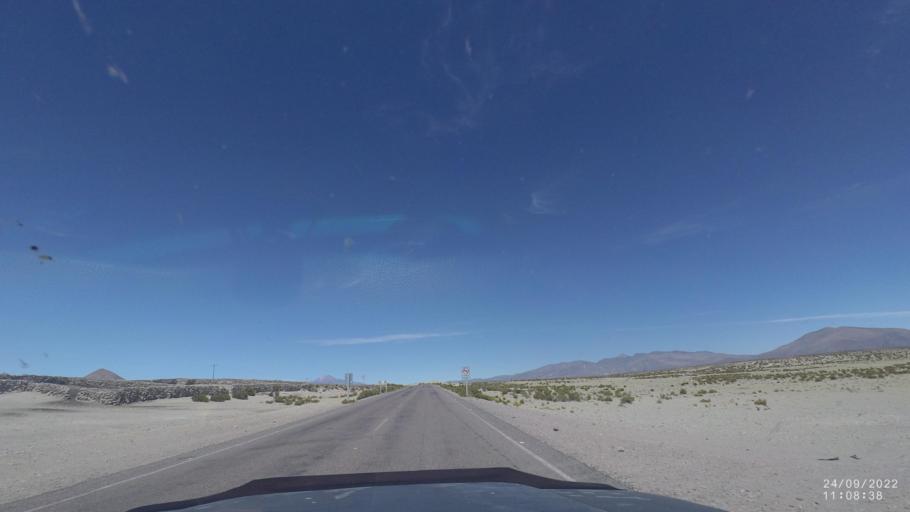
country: BO
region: Oruro
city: Challapata
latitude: -19.4869
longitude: -67.4435
